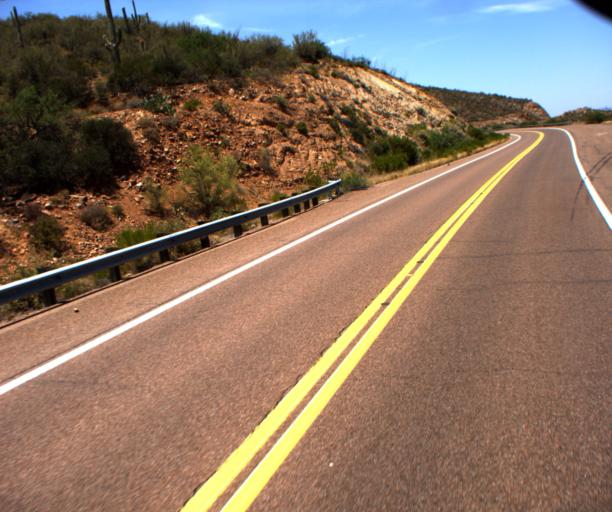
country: US
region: Arizona
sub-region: Gila County
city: Tonto Basin
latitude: 33.6854
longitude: -111.1725
